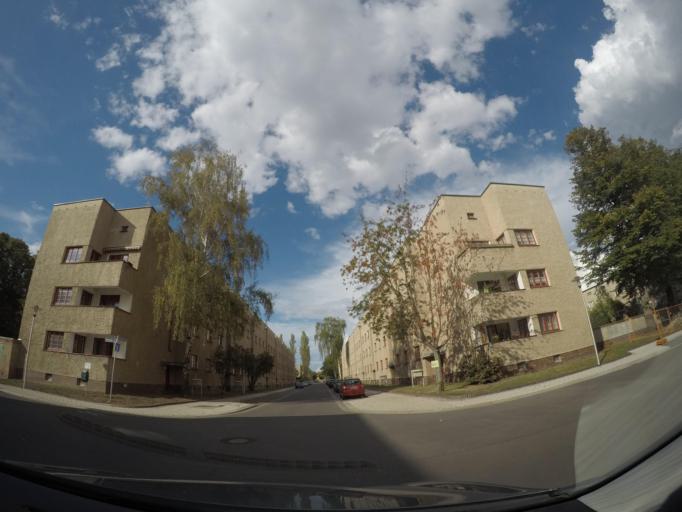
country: DE
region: Saxony-Anhalt
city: Diesdorf
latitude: 52.1252
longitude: 11.5887
